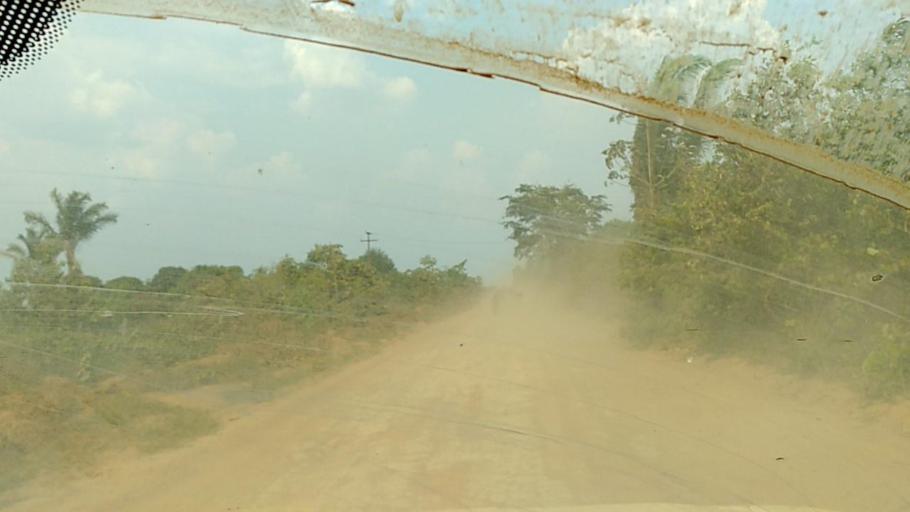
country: BR
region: Rondonia
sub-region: Porto Velho
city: Porto Velho
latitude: -8.6834
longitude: -63.2285
